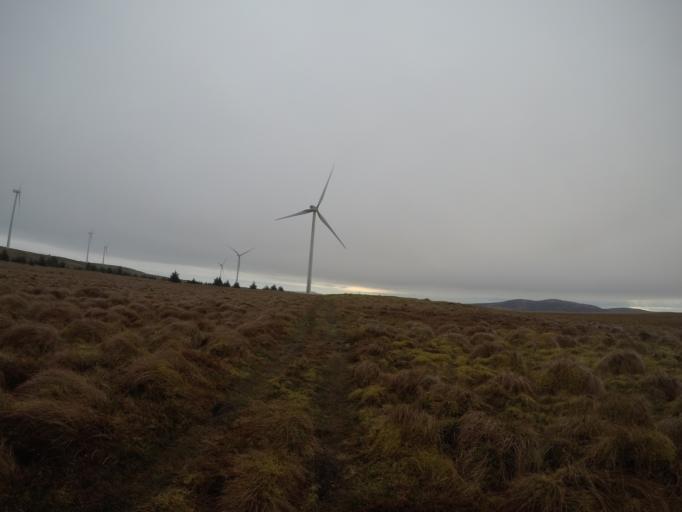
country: GB
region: Scotland
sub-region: North Ayrshire
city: Fairlie
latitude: 55.7388
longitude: -4.7888
